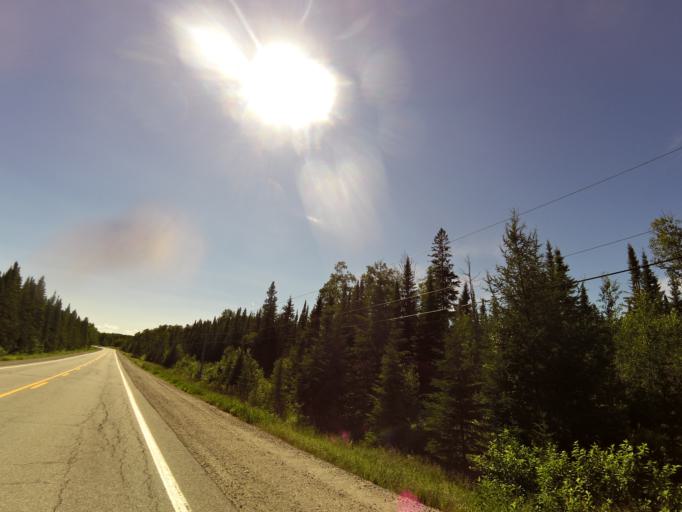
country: CA
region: Quebec
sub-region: Abitibi-Temiscamingue
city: Senneterre
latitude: 48.2274
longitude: -77.3401
